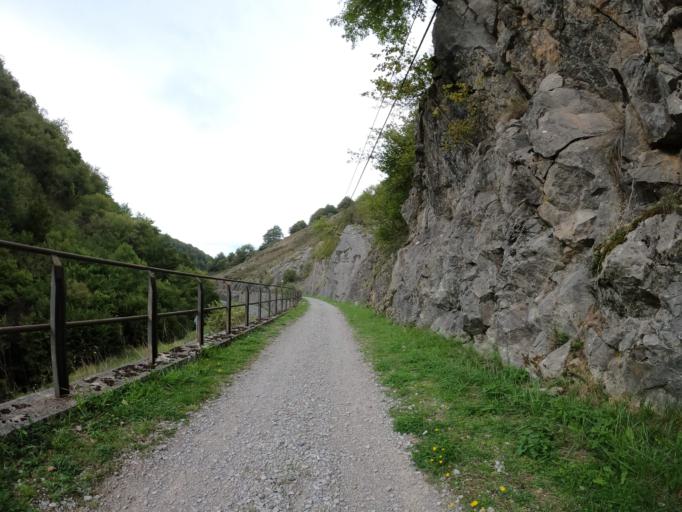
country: ES
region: Navarre
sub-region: Provincia de Navarra
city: Lekunberri
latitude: 43.0210
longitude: -1.9055
